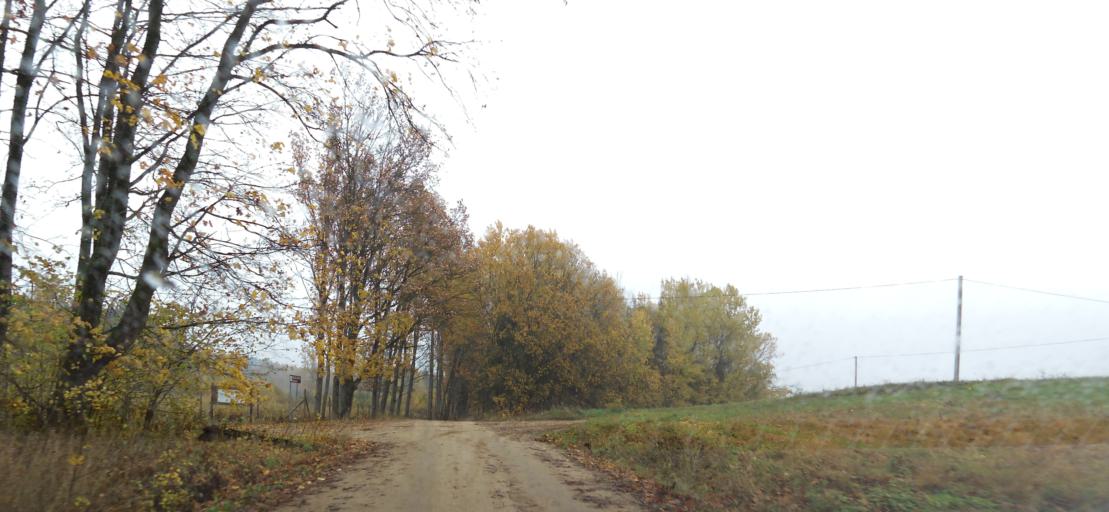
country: LT
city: Skaidiskes
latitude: 54.6273
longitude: 25.4772
